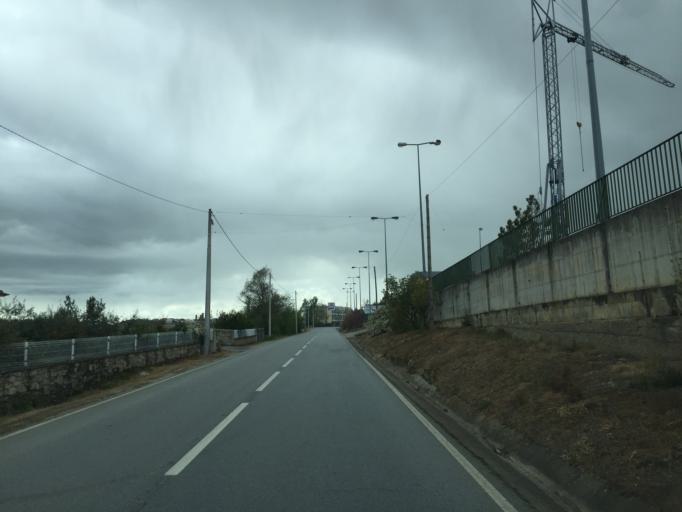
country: PT
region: Braganca
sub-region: Mogadouro
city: Mogadouro
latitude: 41.3421
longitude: -6.7002
